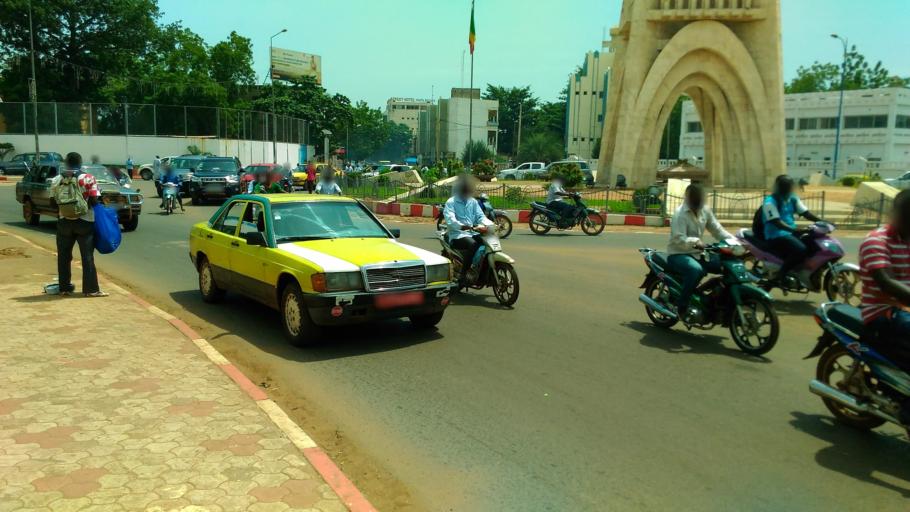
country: ML
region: Bamako
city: Bamako
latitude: 12.6368
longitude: -8.0050
